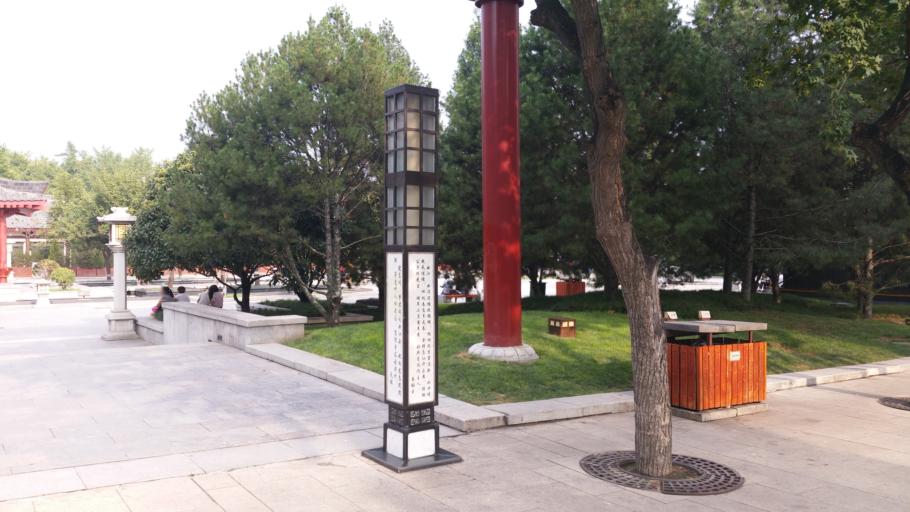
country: CN
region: Shaanxi
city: Yanta
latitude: 34.2185
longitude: 108.9605
